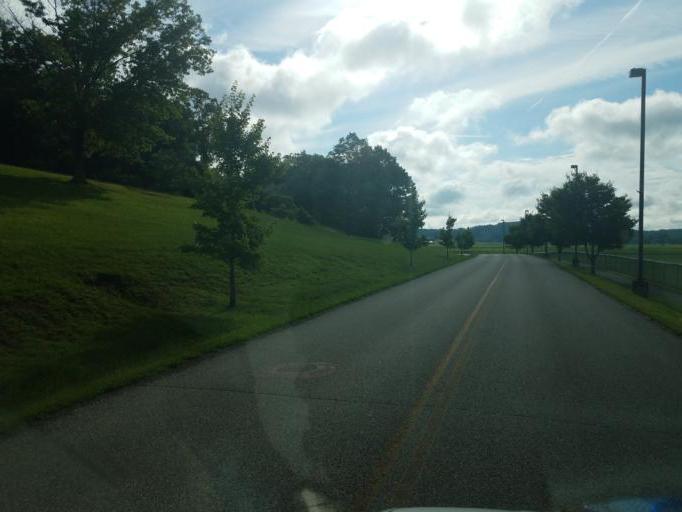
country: US
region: Ohio
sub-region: Gallia County
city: Gallipolis
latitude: 38.8798
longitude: -82.3741
